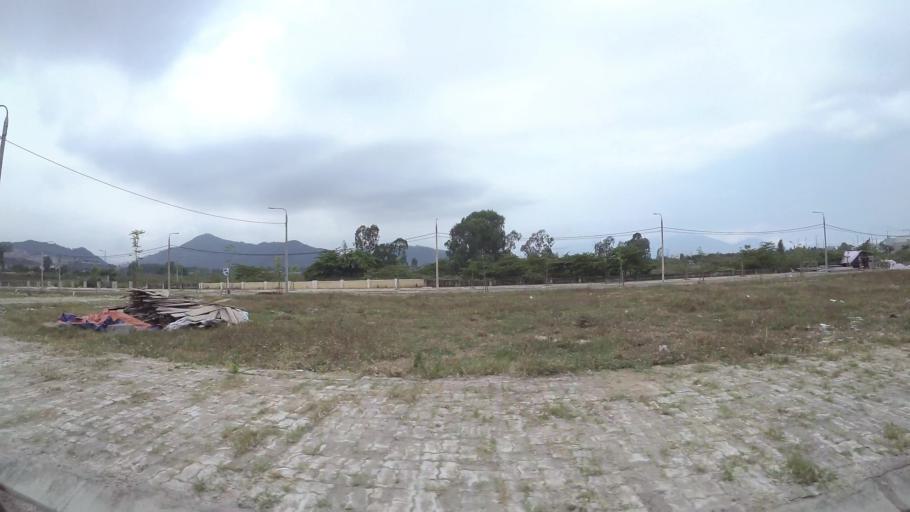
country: VN
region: Da Nang
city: Lien Chieu
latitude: 16.0440
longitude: 108.1642
